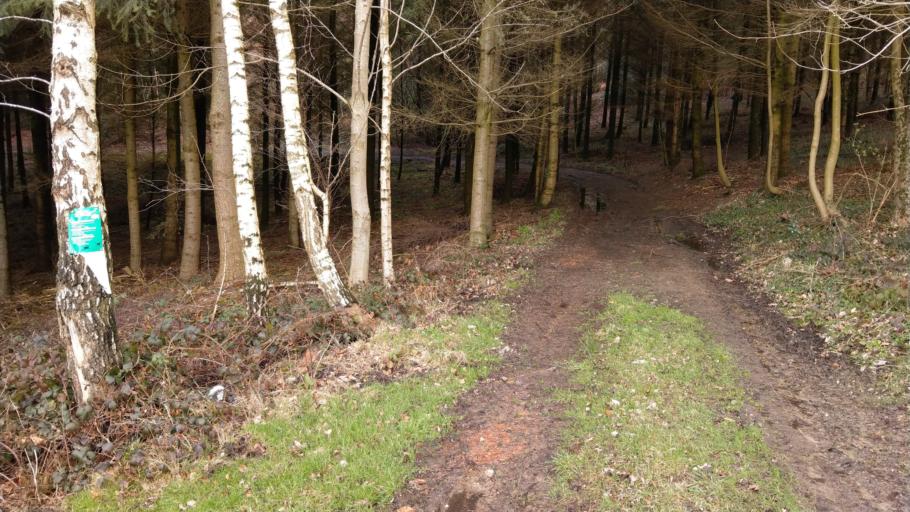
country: BE
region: Wallonia
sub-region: Province de Liege
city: Plombieres
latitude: 50.7587
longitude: 5.9639
